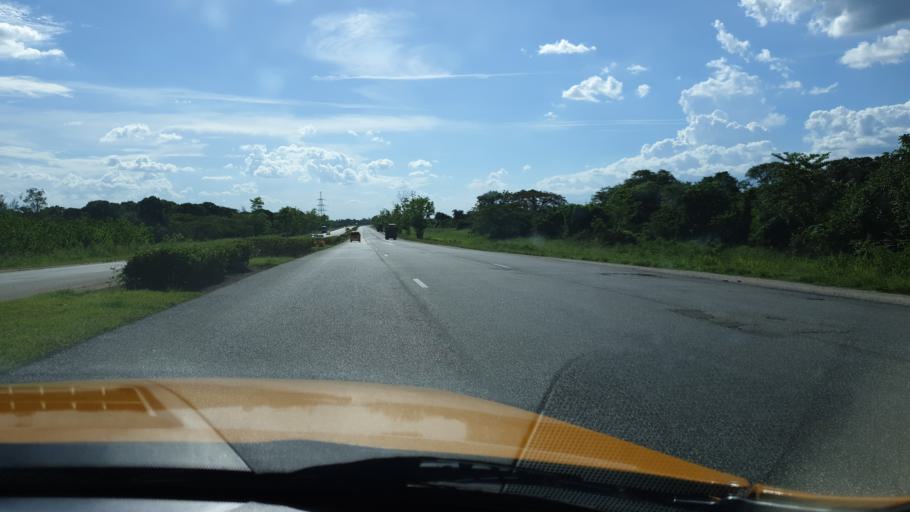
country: CU
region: Cienfuegos
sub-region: Municipio de Aguada de Pasajeros
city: Aguada de Pasajeros
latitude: 22.4073
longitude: -80.8791
